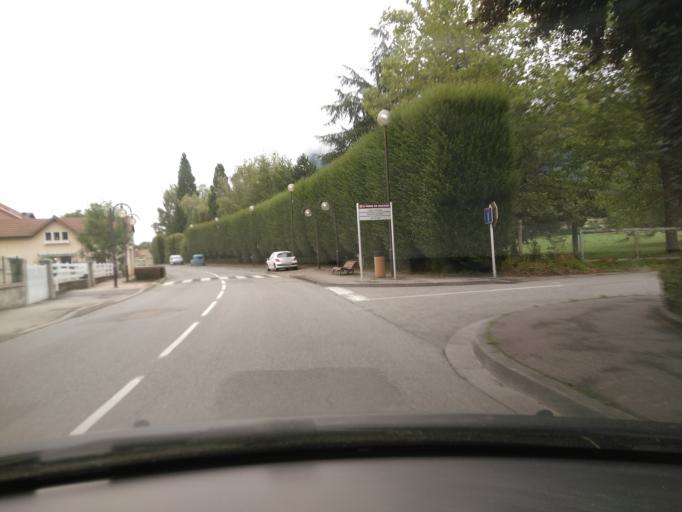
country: FR
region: Rhone-Alpes
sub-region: Departement de la Haute-Savoie
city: Amancy
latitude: 46.0594
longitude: 6.3698
